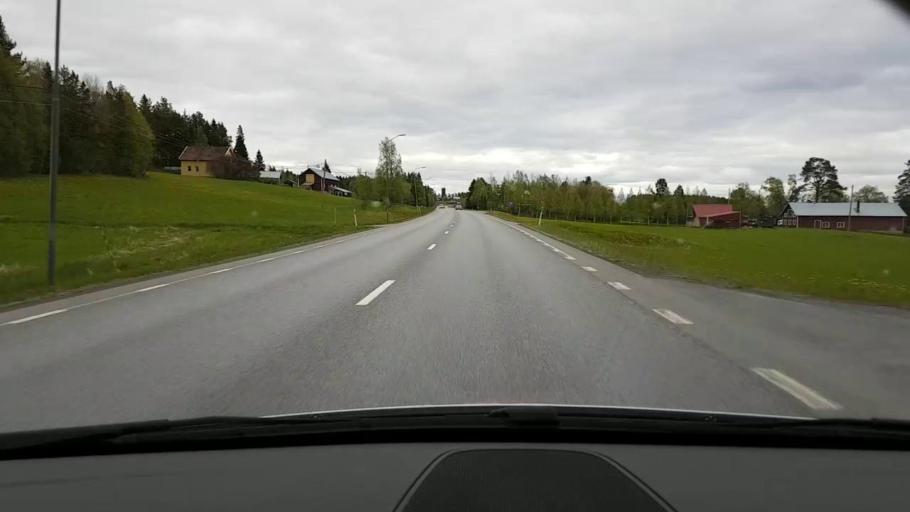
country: SE
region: Jaemtland
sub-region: Krokoms Kommun
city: Valla
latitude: 63.3200
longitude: 14.0703
